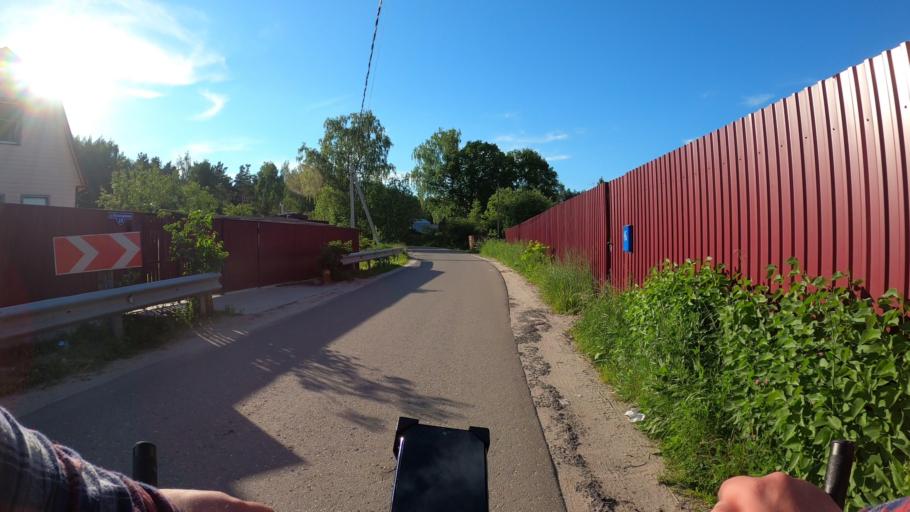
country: RU
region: Moskovskaya
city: Ashitkovo
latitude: 55.4406
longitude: 38.6020
